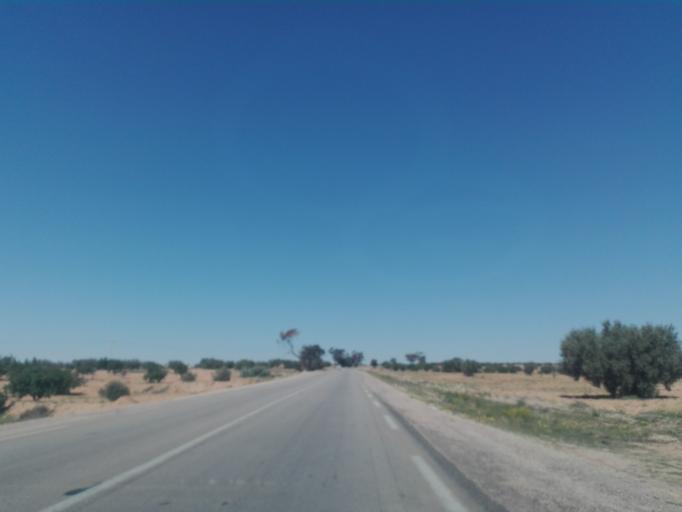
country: TN
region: Safaqis
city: Bi'r `Ali Bin Khalifah
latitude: 34.7464
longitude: 10.3592
